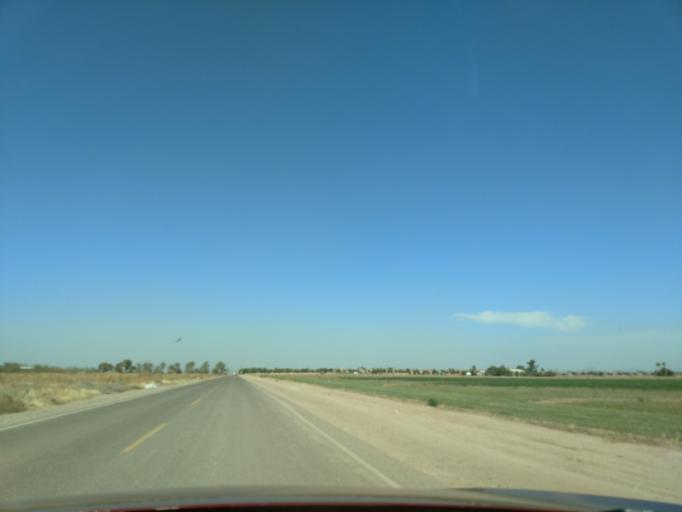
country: US
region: Arizona
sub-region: Maricopa County
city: Laveen
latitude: 33.3561
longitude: -112.1863
